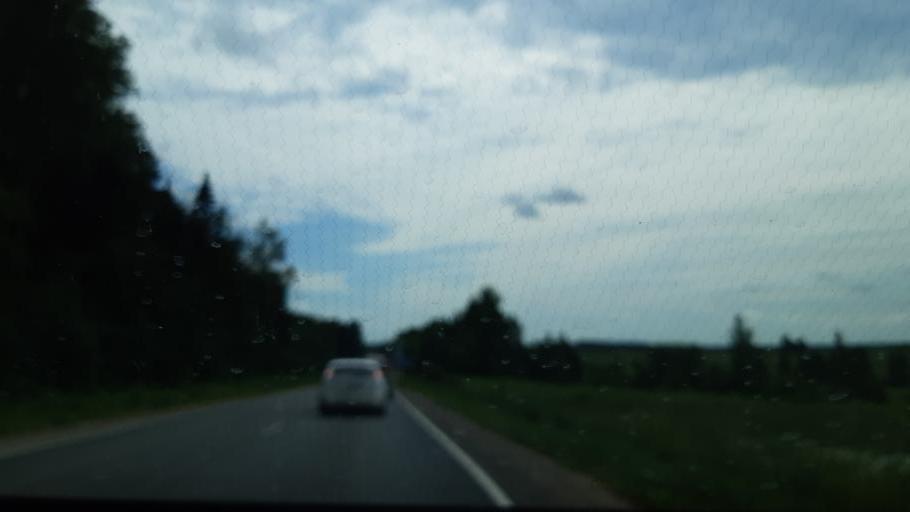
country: RU
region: Moskovskaya
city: Vereya
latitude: 55.3974
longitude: 36.3219
